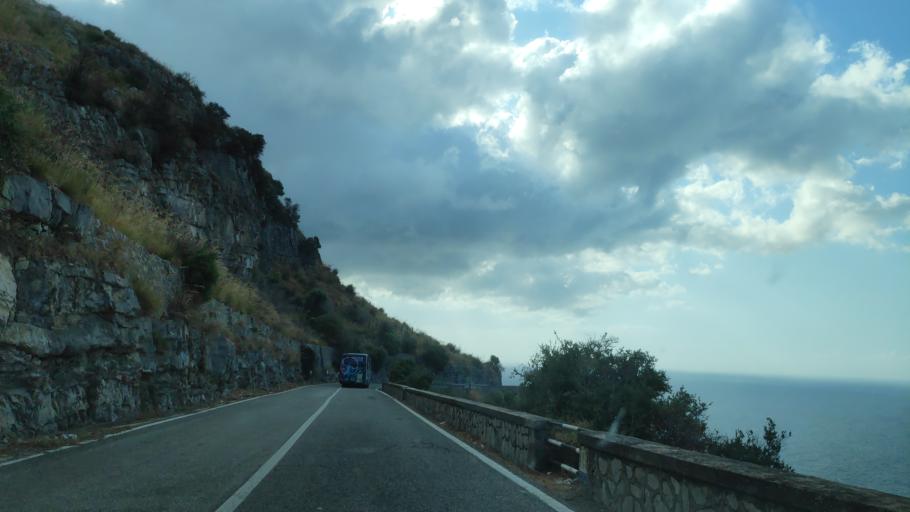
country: IT
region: Campania
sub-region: Provincia di Salerno
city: Positano
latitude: 40.6188
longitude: 14.4610
